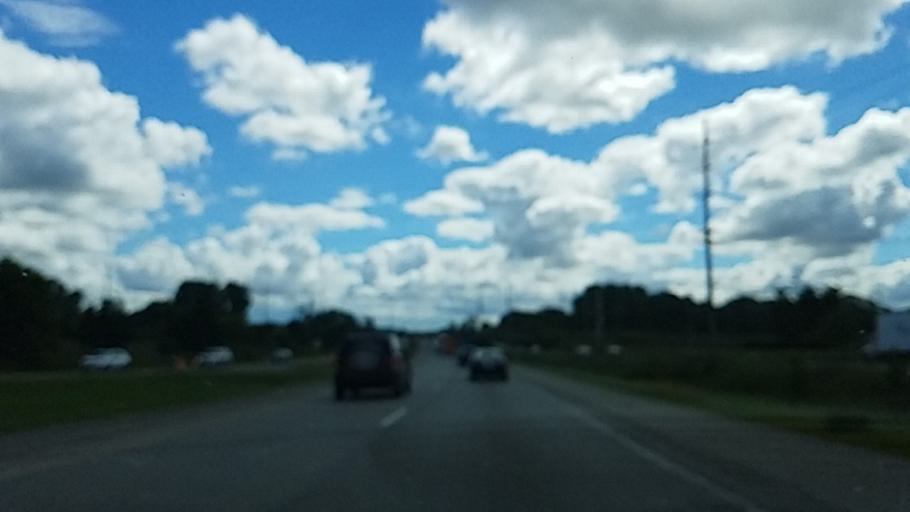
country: US
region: Michigan
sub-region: Livingston County
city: Brighton
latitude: 42.5143
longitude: -83.7585
